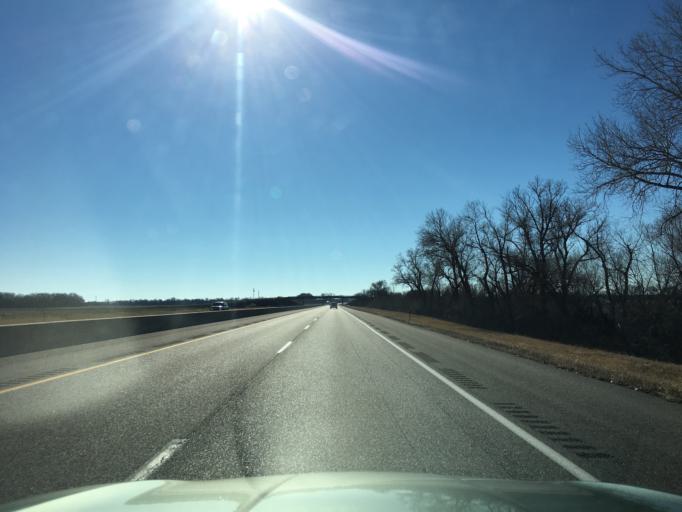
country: US
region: Kansas
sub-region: Sumner County
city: Belle Plaine
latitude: 37.4251
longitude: -97.3213
